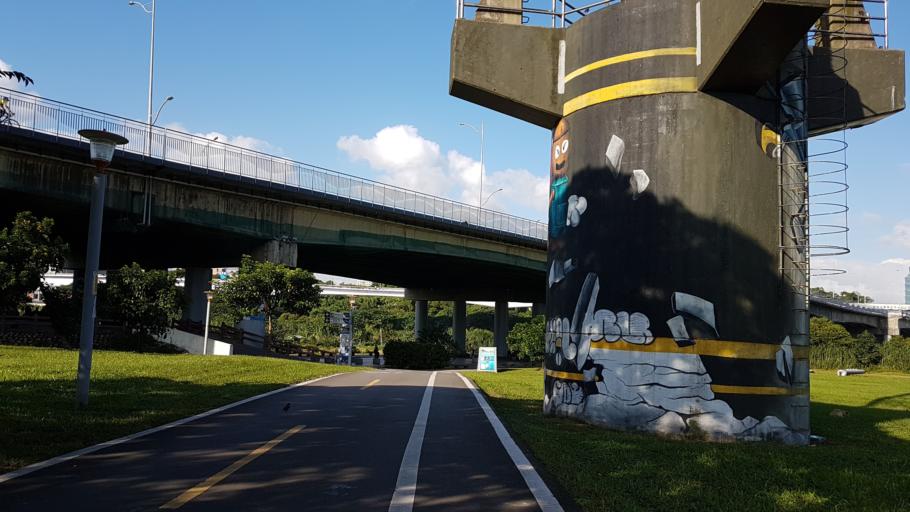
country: TW
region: Taipei
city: Taipei
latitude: 25.0068
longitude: 121.5299
